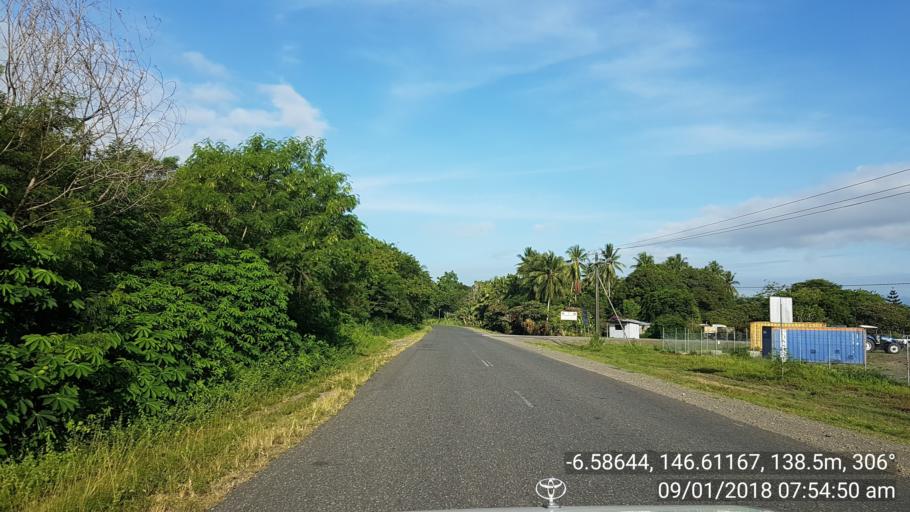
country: PG
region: Morobe
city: Lae
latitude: -6.5867
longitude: 146.6119
